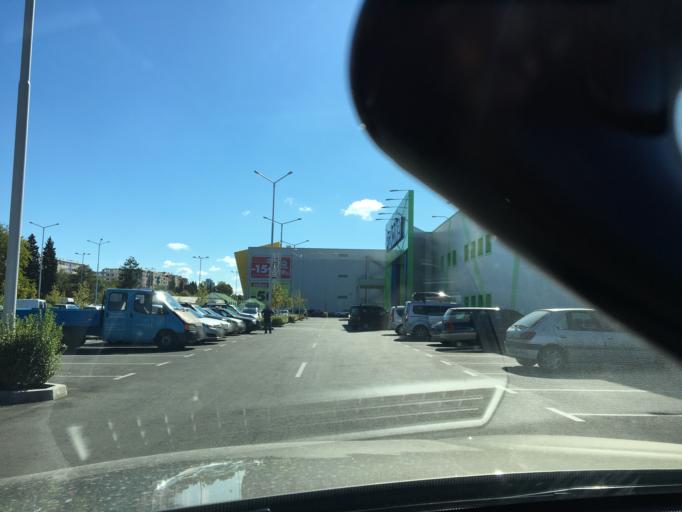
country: BG
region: Burgas
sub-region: Obshtina Burgas
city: Burgas
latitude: 42.5144
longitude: 27.4510
